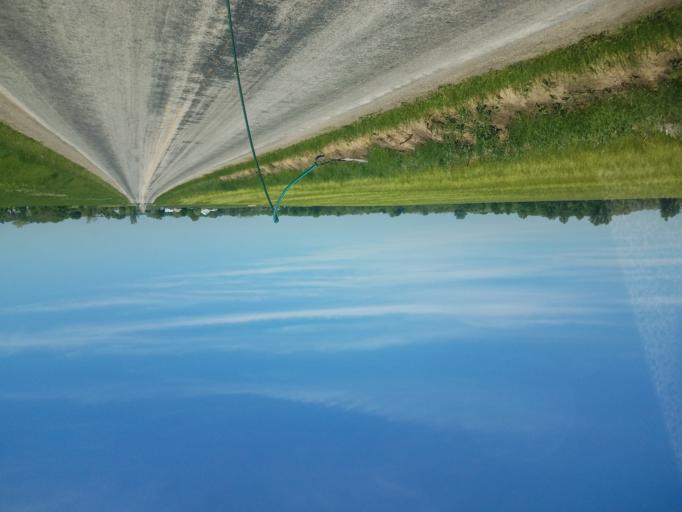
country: US
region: Ohio
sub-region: Ashland County
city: Ashland
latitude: 40.9235
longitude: -82.2433
